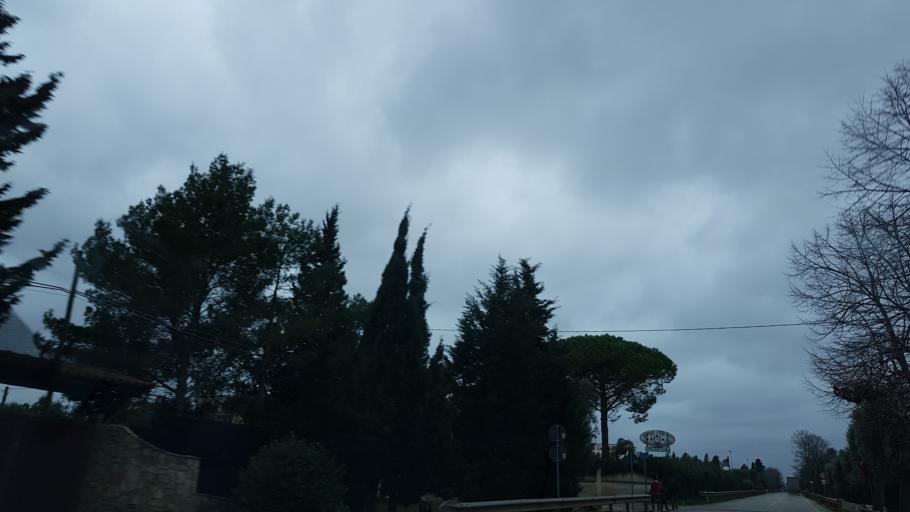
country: IT
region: Apulia
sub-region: Provincia di Brindisi
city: San Vito dei Normanni
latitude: 40.6563
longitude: 17.7412
